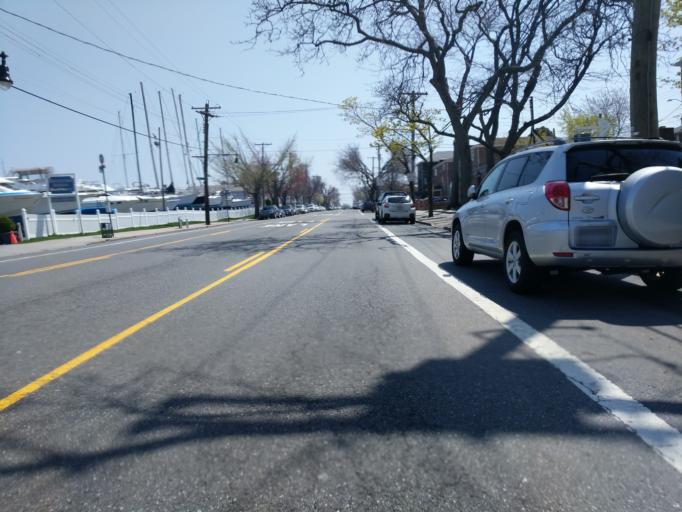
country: US
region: New York
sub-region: Nassau County
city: Kings Point
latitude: 40.8430
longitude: -73.7850
